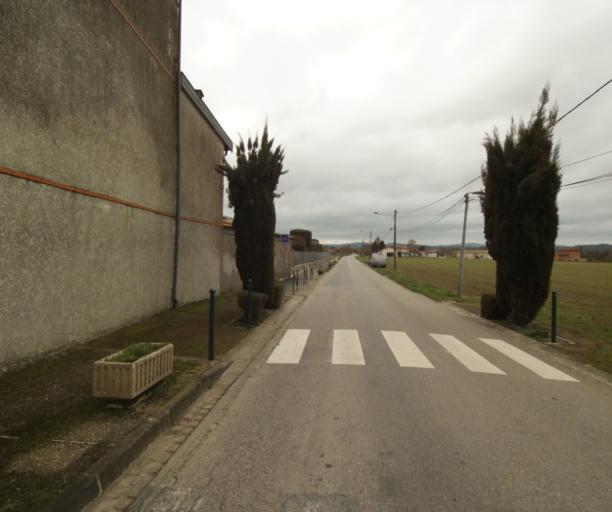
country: FR
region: Midi-Pyrenees
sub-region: Departement de l'Ariege
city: La Tour-du-Crieu
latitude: 43.1532
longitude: 1.6367
